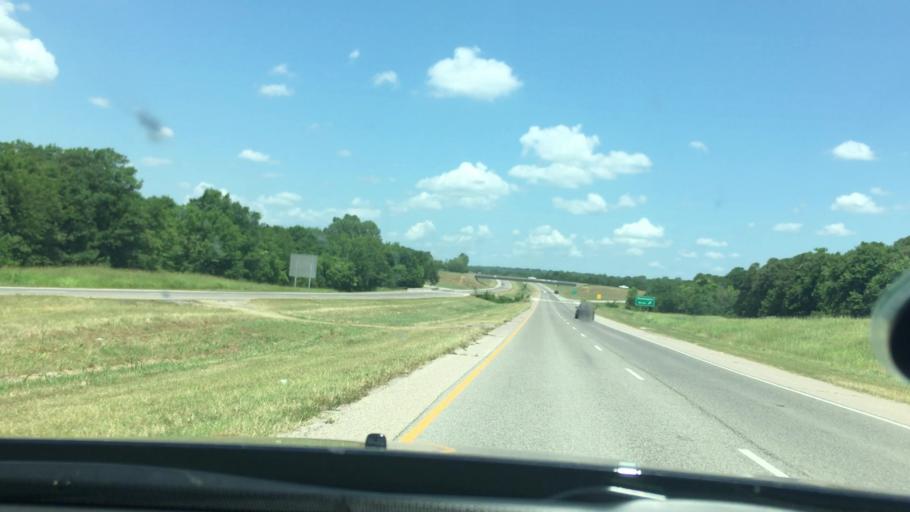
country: US
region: Oklahoma
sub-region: Pontotoc County
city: Ada
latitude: 34.7336
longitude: -96.6414
